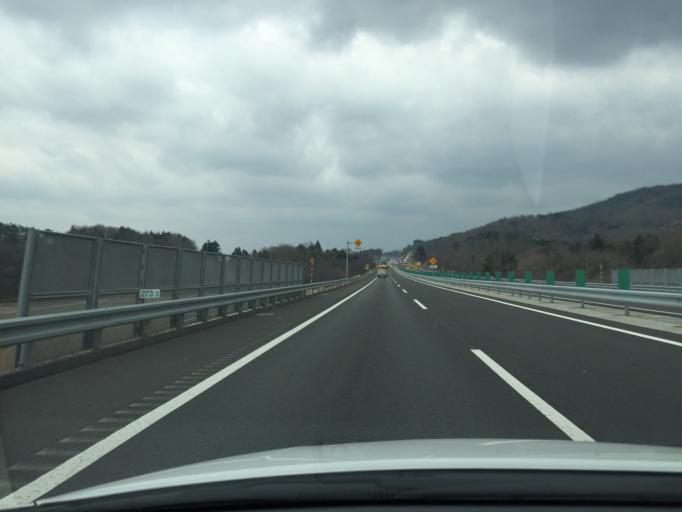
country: JP
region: Miyagi
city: Marumori
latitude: 37.8474
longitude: 140.8797
